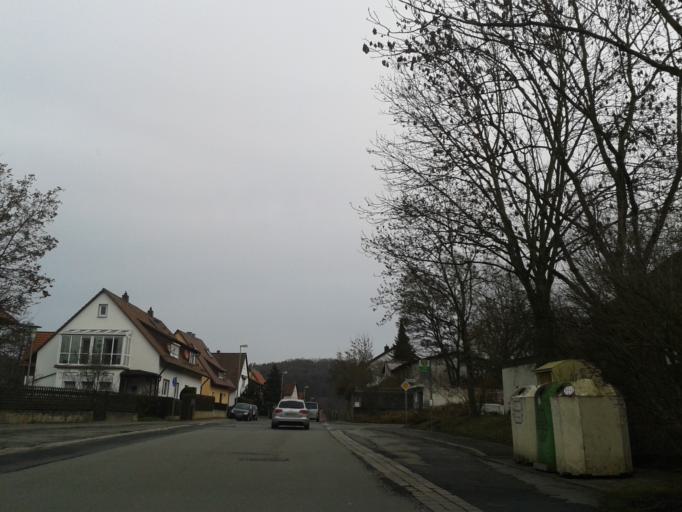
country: DE
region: Bavaria
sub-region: Upper Franconia
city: Niederfullbach
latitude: 50.2479
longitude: 10.9967
